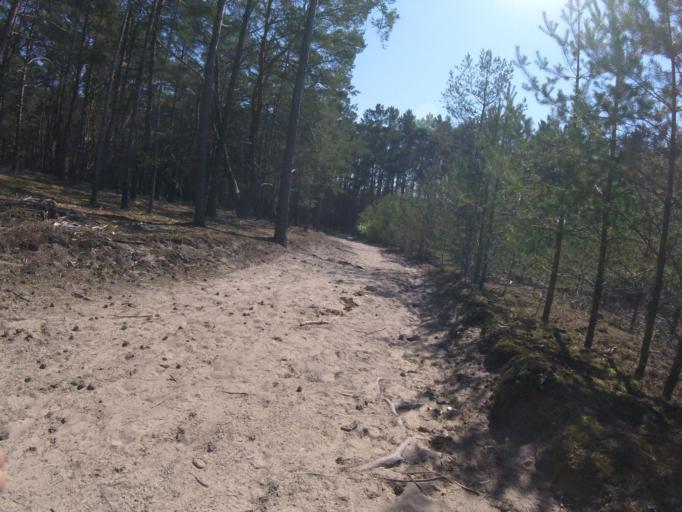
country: DE
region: Brandenburg
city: Bestensee
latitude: 52.2655
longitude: 13.6823
